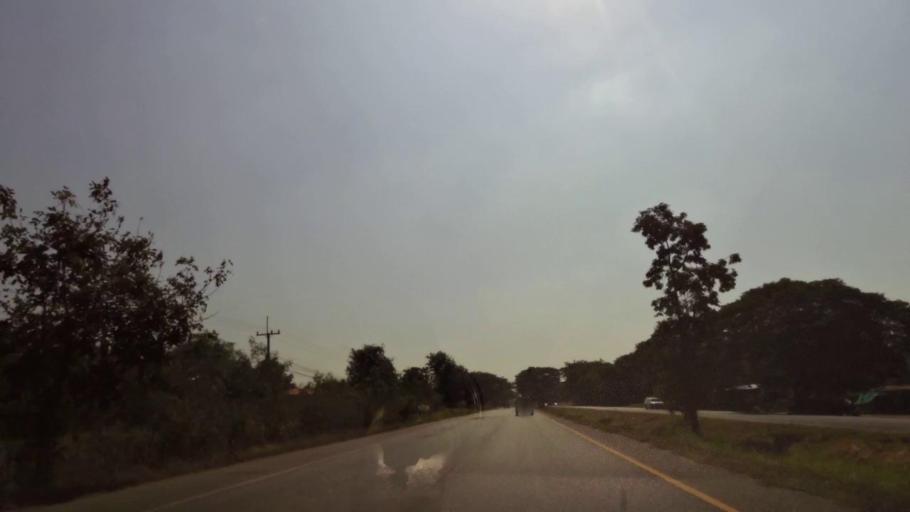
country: TH
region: Phichit
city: Bueng Na Rang
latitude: 16.3404
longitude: 100.1283
